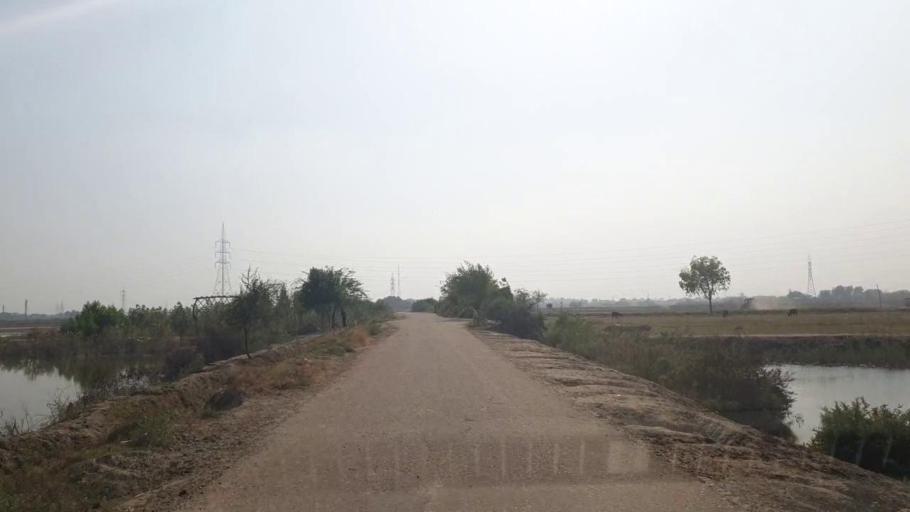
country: PK
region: Sindh
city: Jamshoro
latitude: 25.4577
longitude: 68.3368
